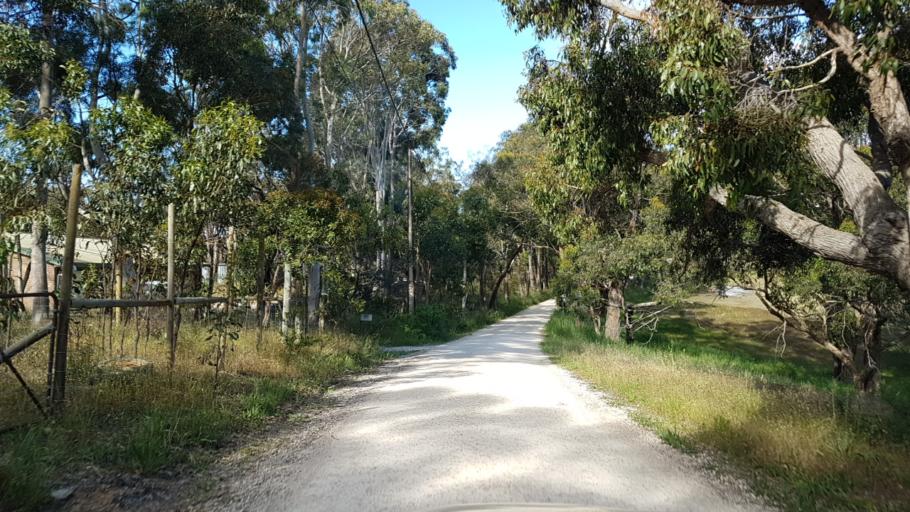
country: AU
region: South Australia
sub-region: Adelaide Hills
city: Adelaide Hills
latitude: -34.9054
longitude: 138.7404
